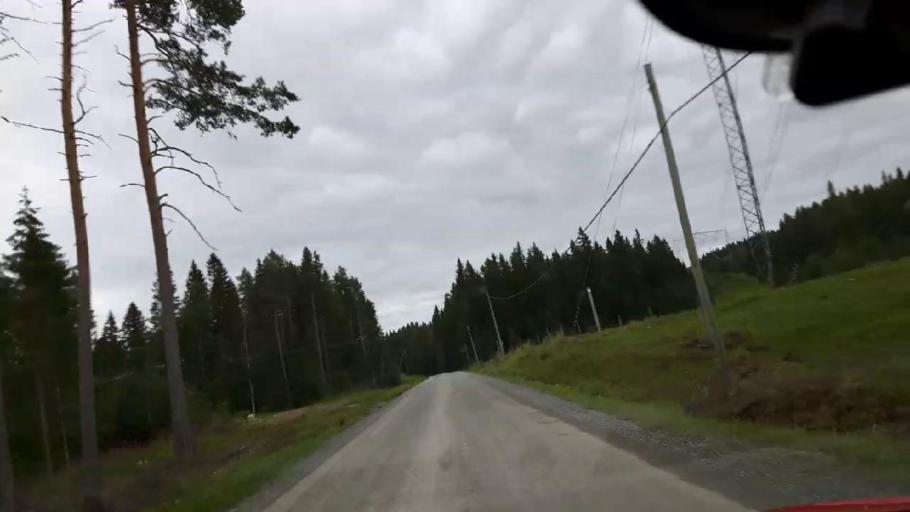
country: SE
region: Jaemtland
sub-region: Braecke Kommun
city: Braecke
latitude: 63.0797
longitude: 15.2866
